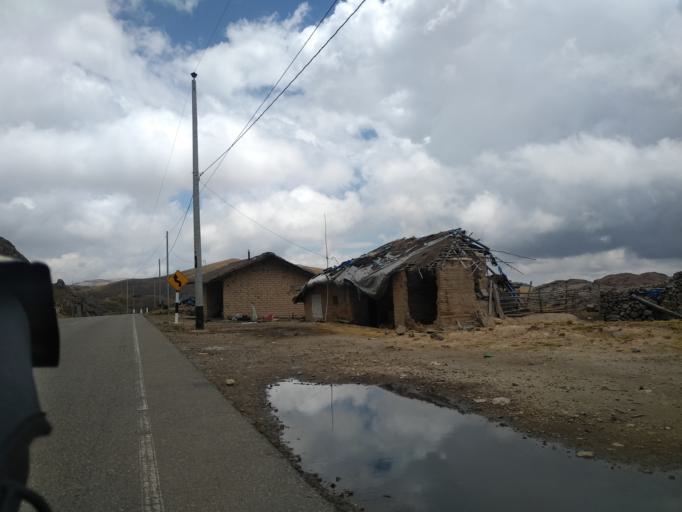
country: PE
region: La Libertad
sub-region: Provincia de Santiago de Chuco
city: Quiruvilca
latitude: -7.9741
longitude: -78.2139
